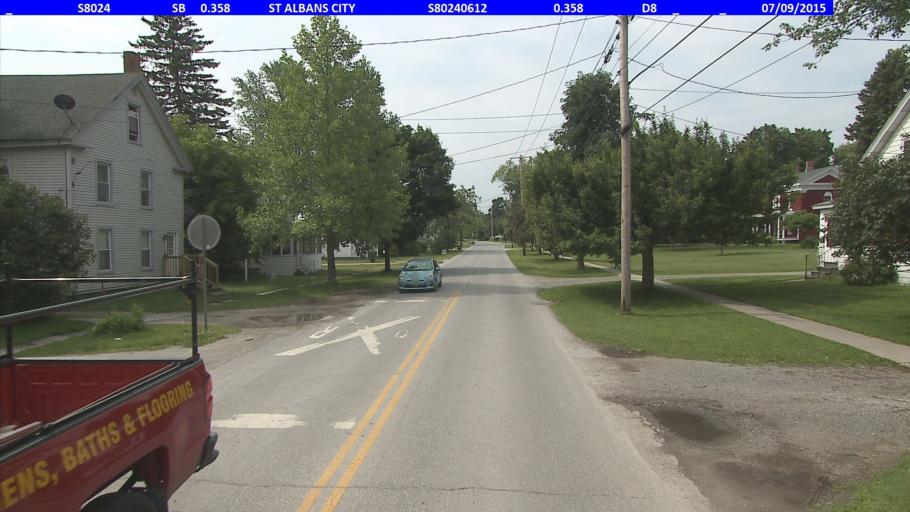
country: US
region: Vermont
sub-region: Franklin County
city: Saint Albans
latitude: 44.8162
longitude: -73.0913
